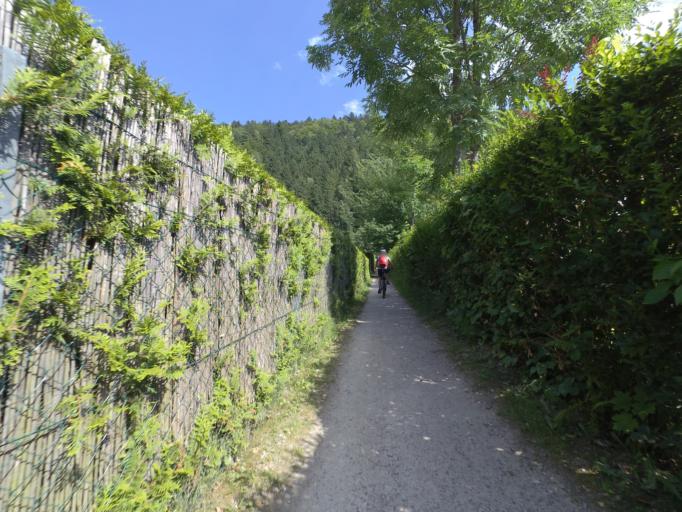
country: AT
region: Carinthia
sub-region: Politischer Bezirk Villach Land
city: Ferndorf
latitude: 46.7685
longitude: 13.6481
